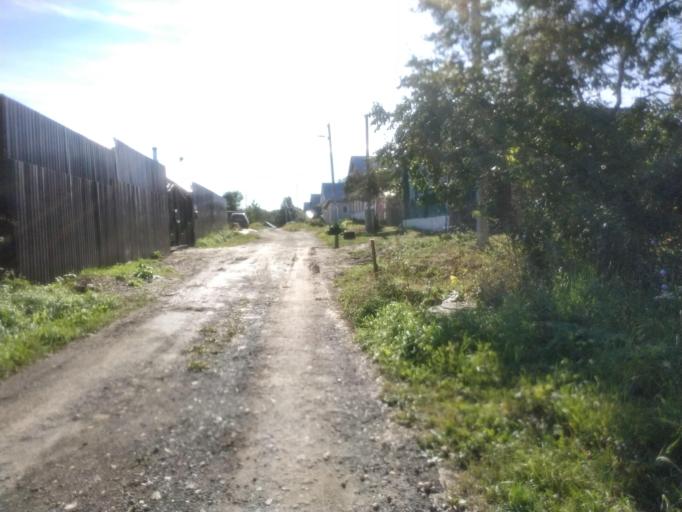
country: RU
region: Chuvashia
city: Novyye Lapsary
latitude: 56.1440
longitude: 47.1487
